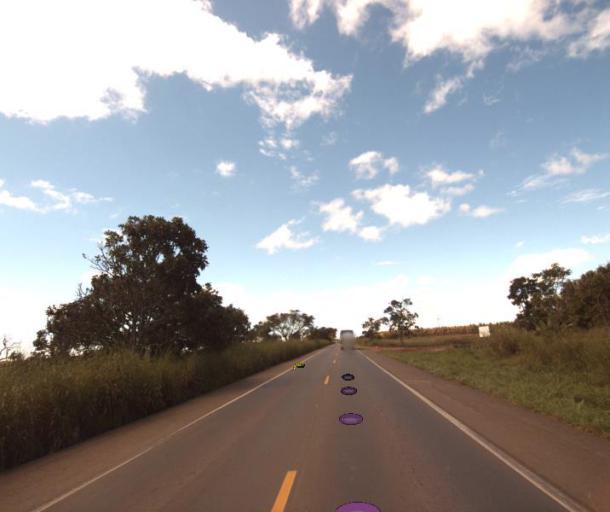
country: BR
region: Goias
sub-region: Rialma
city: Rialma
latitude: -15.4627
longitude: -49.5003
